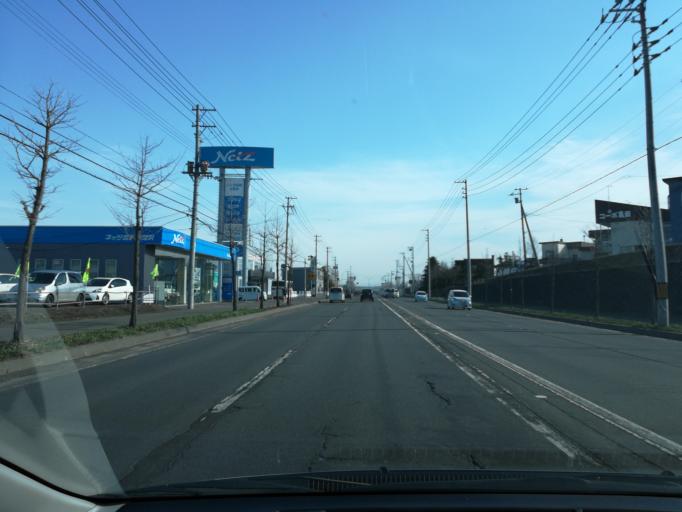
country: JP
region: Hokkaido
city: Iwamizawa
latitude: 43.2167
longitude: 141.7858
